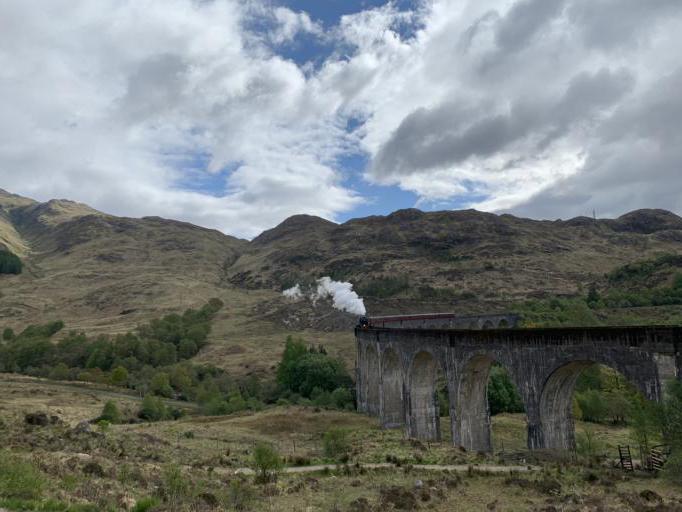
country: GB
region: Scotland
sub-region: Highland
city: Fort William
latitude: 56.8762
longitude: -5.4345
